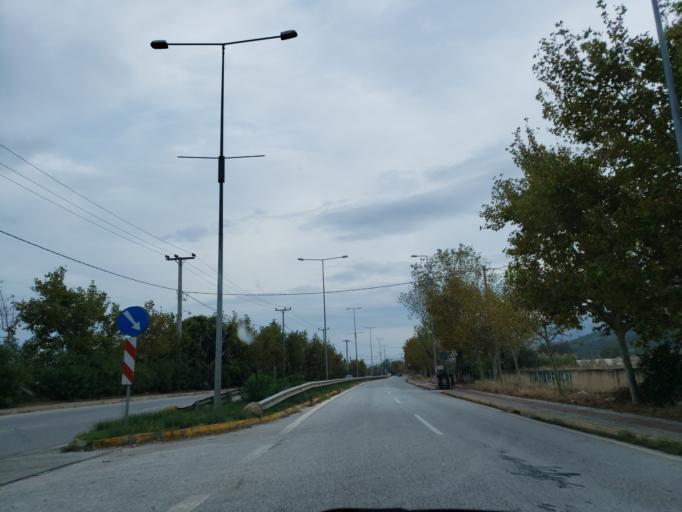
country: GR
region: Attica
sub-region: Nomarchia Anatolikis Attikis
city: Marathonas
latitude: 38.1411
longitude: 23.9661
